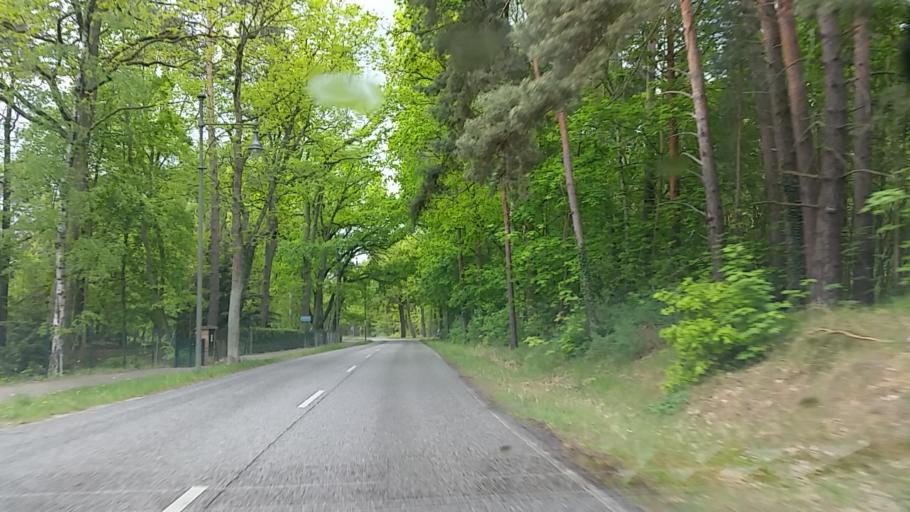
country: DE
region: Brandenburg
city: Diensdorf-Radlow
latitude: 52.2723
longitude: 14.0398
